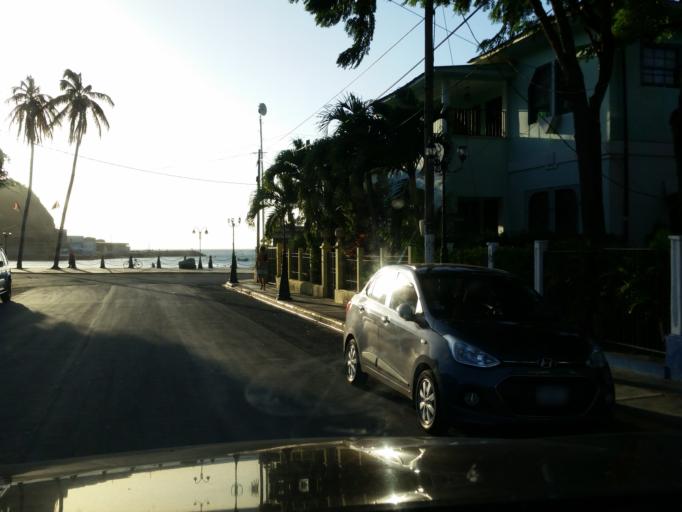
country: NI
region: Rivas
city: San Juan del Sur
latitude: 11.2523
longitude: -85.8720
